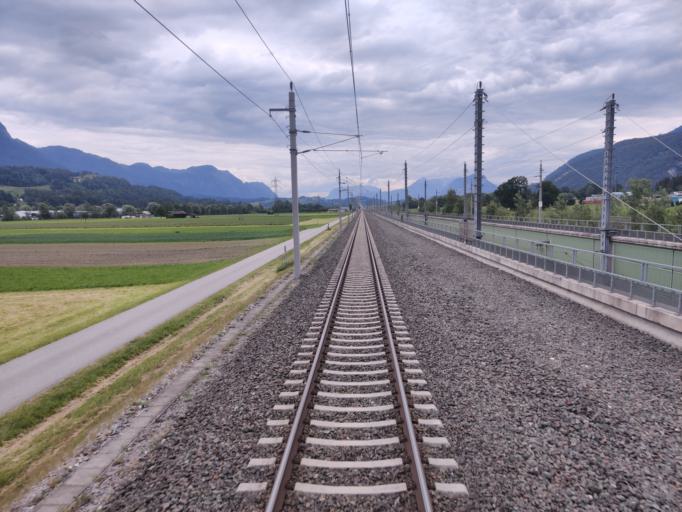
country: AT
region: Tyrol
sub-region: Politischer Bezirk Kufstein
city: Radfeld
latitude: 47.4519
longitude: 11.9281
